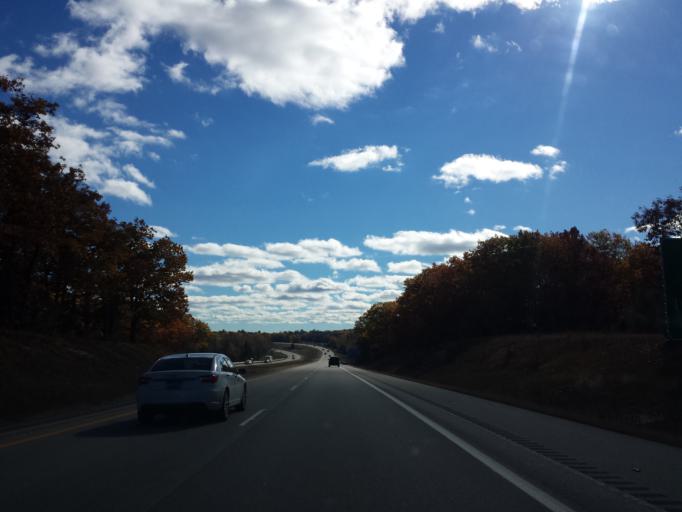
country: US
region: Michigan
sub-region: Cheboygan County
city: Indian River
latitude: 45.4629
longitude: -84.6159
